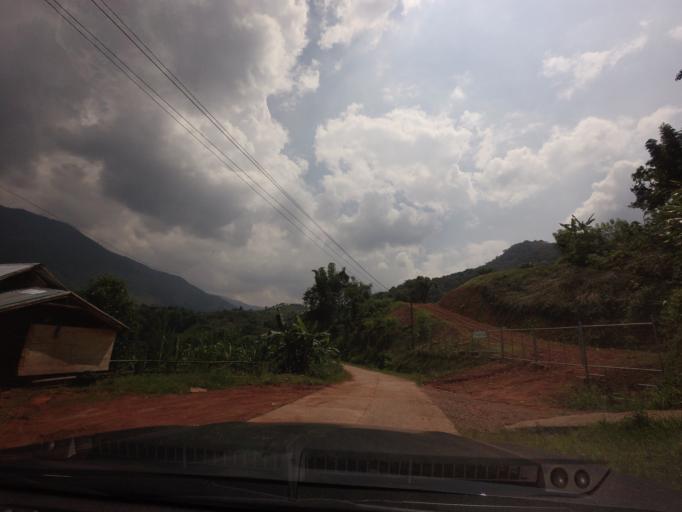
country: TH
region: Nan
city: Bo Kluea
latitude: 19.1883
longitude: 101.2008
